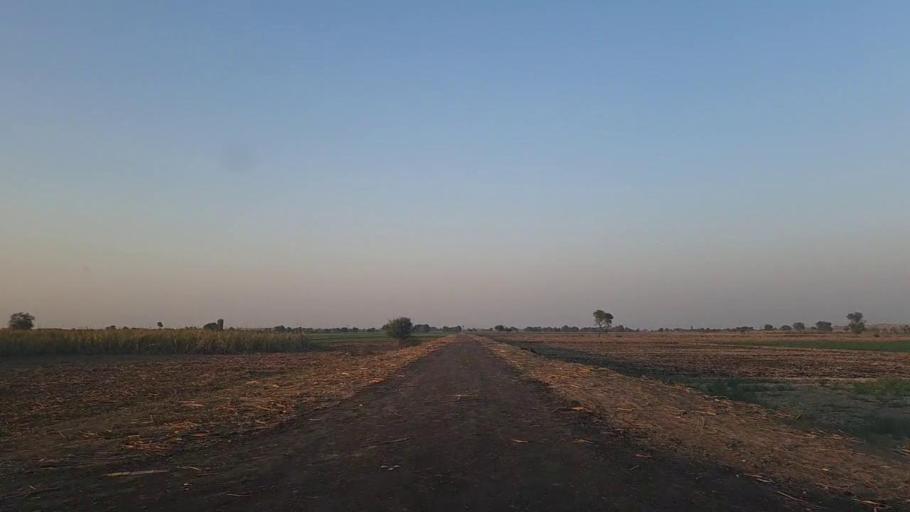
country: PK
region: Sindh
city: Jam Sahib
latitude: 26.3550
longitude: 68.7186
